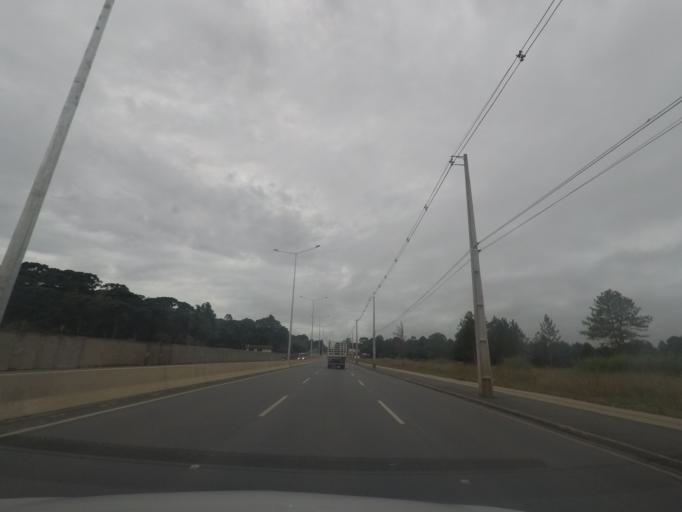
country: BR
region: Parana
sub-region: Piraquara
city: Piraquara
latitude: -25.4530
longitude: -49.1168
